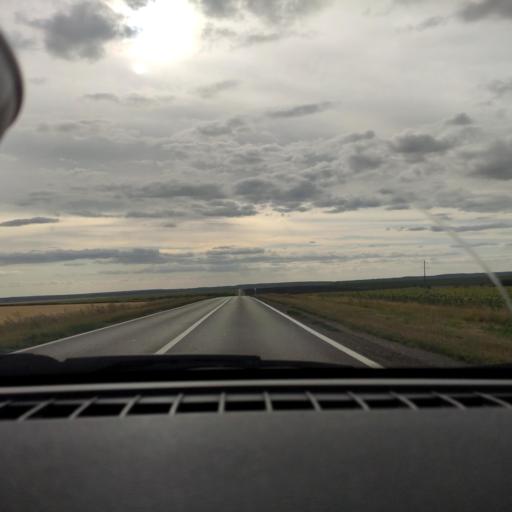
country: RU
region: Samara
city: Georgiyevka
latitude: 53.4174
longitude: 50.9222
